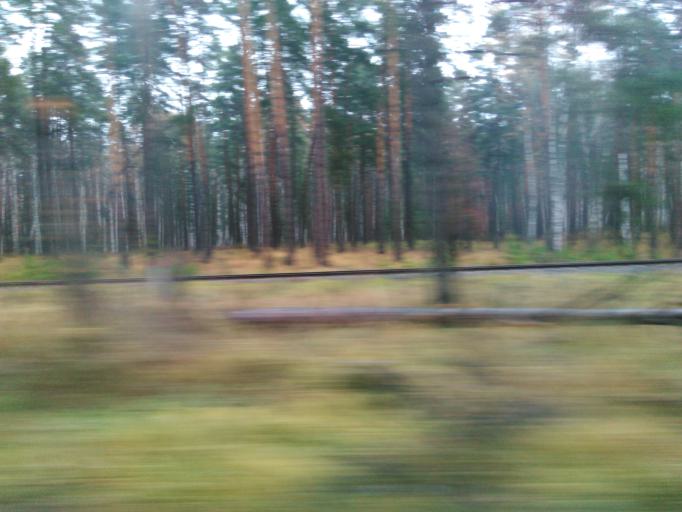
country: RU
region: Tatarstan
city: Osinovo
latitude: 55.8282
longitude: 48.8950
